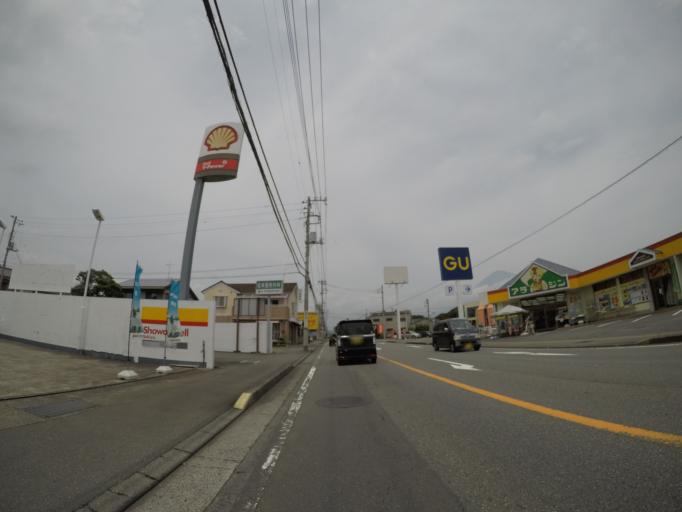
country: JP
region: Shizuoka
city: Fujinomiya
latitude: 35.2350
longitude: 138.6092
